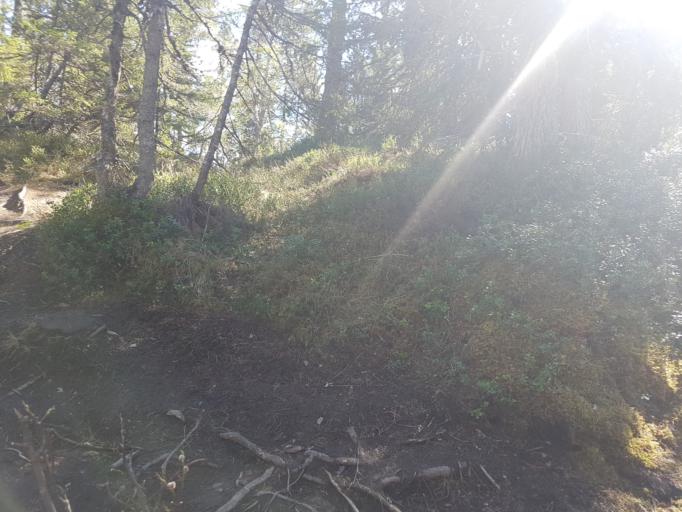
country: NO
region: Sor-Trondelag
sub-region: Trondheim
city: Trondheim
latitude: 63.4269
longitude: 10.3149
